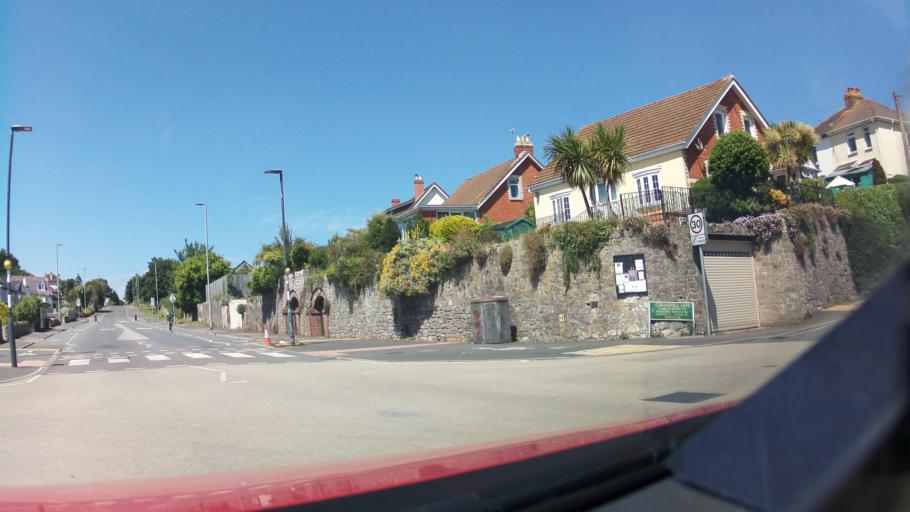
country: GB
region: England
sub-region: Devon
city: Kingskerswell
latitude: 50.5001
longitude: -3.5790
